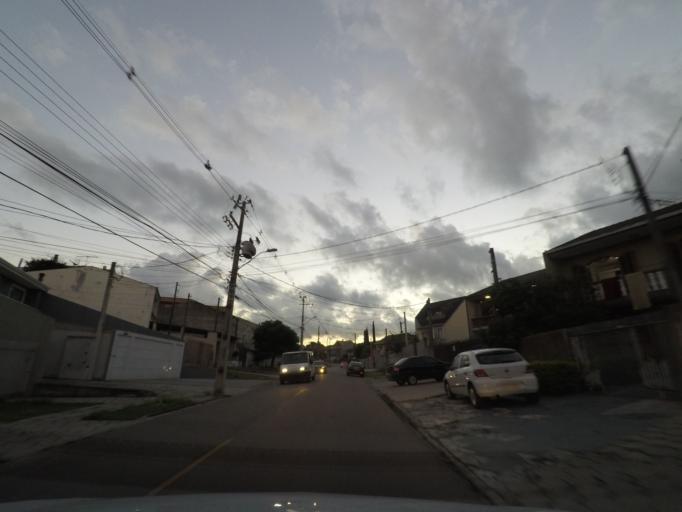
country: BR
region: Parana
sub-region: Sao Jose Dos Pinhais
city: Sao Jose dos Pinhais
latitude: -25.4981
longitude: -49.2641
